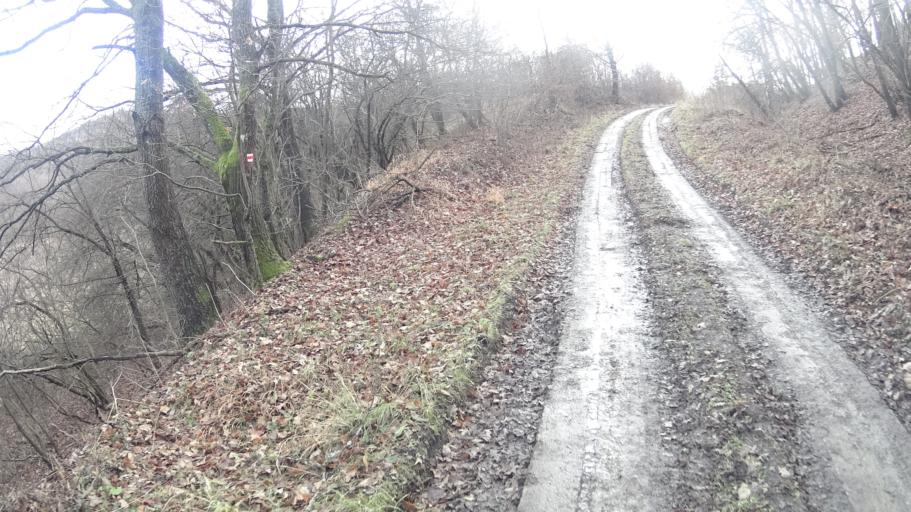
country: HU
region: Pest
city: Nagymaros
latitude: 47.8499
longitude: 18.9427
